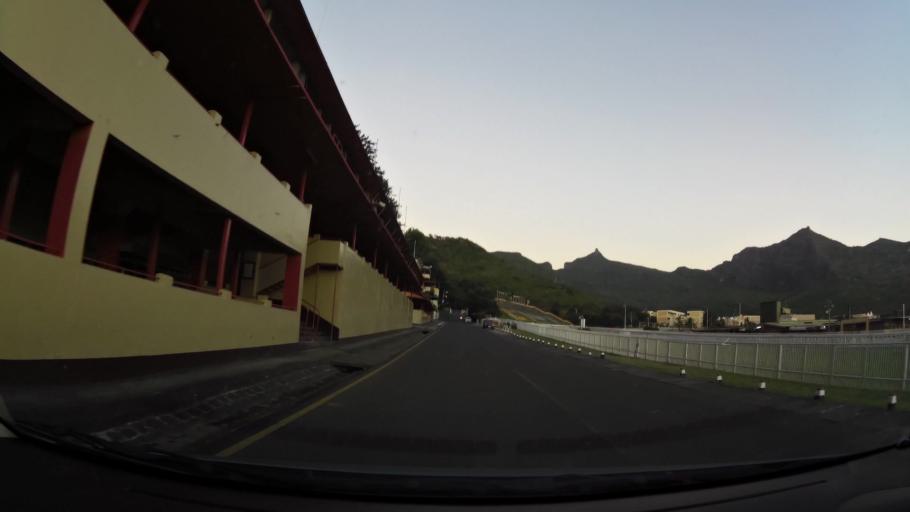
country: MU
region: Port Louis
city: Port Louis
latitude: -20.1682
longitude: 57.5118
